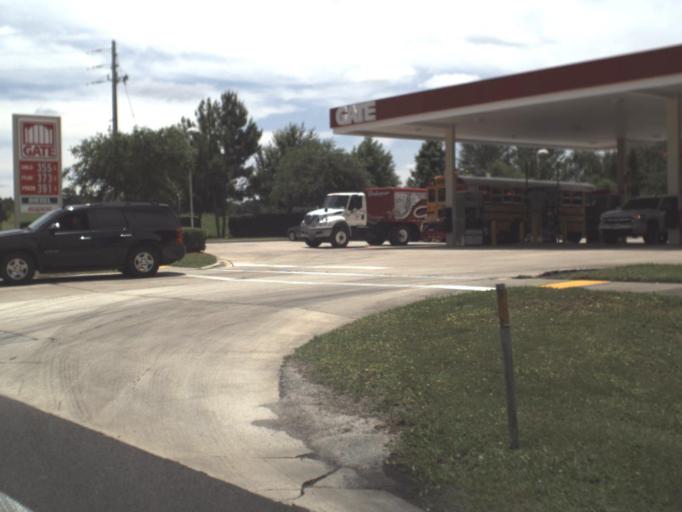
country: US
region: Florida
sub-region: Nassau County
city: Nassau Village-Ratliff
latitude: 30.4343
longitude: -81.7612
